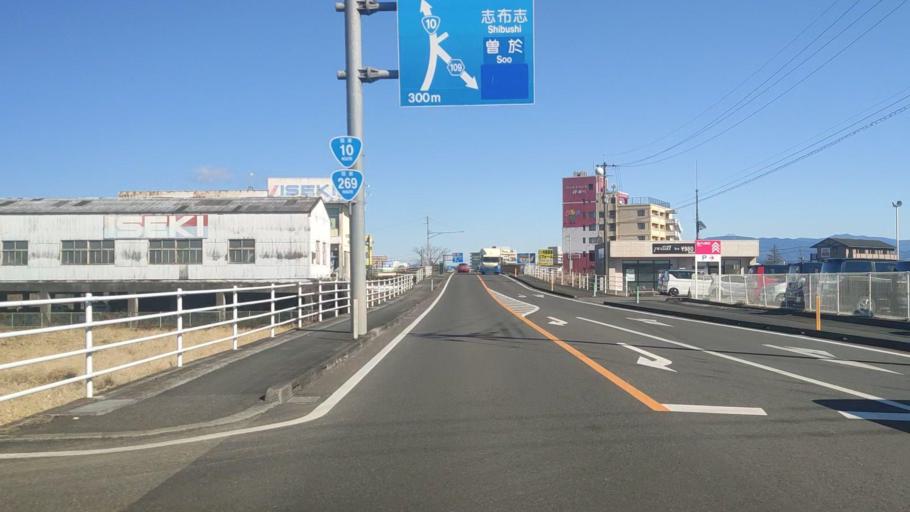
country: JP
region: Miyazaki
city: Miyakonojo
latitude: 31.7121
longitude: 131.0577
